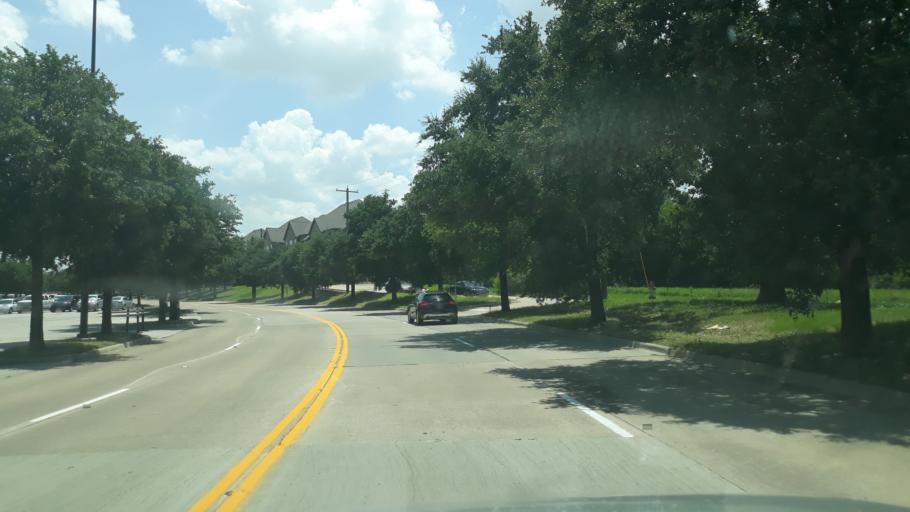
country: US
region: Texas
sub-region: Dallas County
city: Coppell
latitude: 32.9676
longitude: -97.0456
